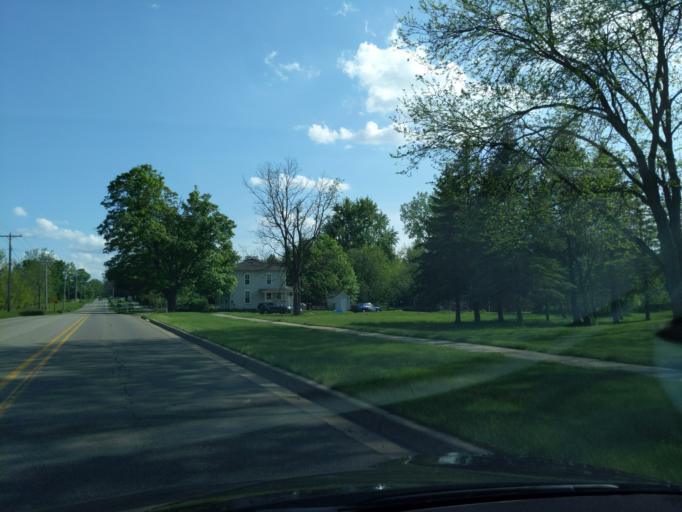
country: US
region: Michigan
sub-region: Ingham County
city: Okemos
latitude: 42.6972
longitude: -84.4104
